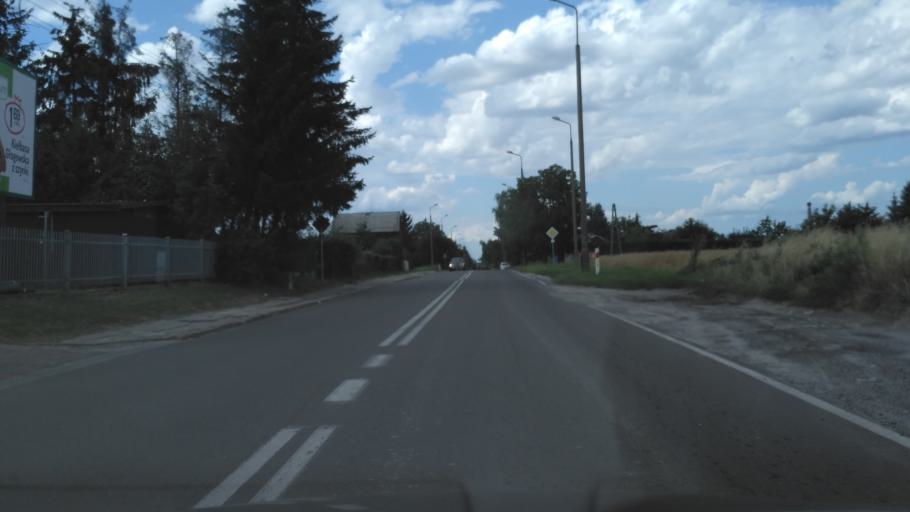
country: PL
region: Lublin Voivodeship
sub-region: Powiat leczynski
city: Milejow
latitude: 51.2122
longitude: 22.9319
